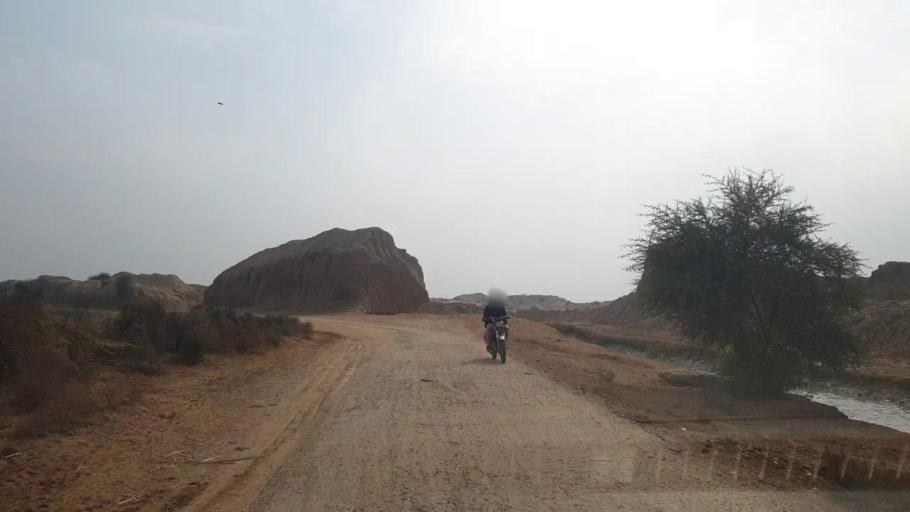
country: PK
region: Sindh
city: Sann
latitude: 26.0165
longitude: 68.1445
